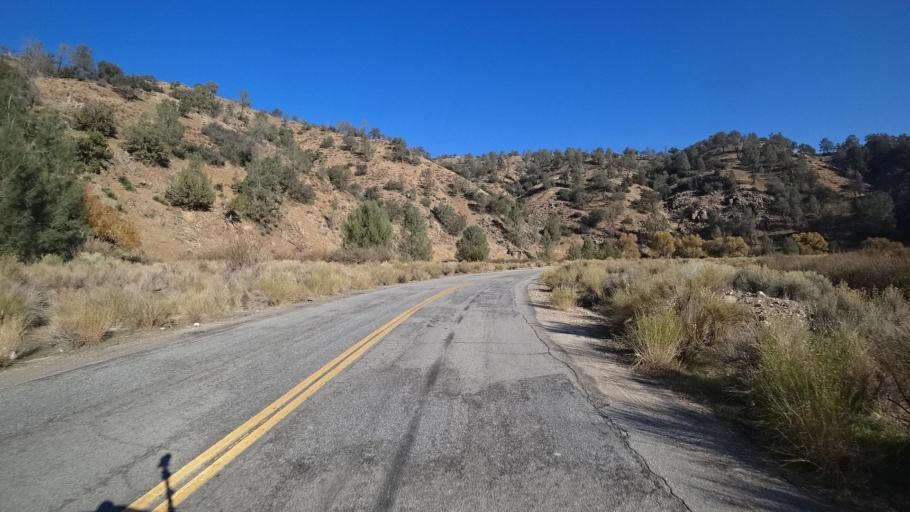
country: US
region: California
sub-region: Kern County
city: Golden Hills
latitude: 35.3057
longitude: -118.4529
